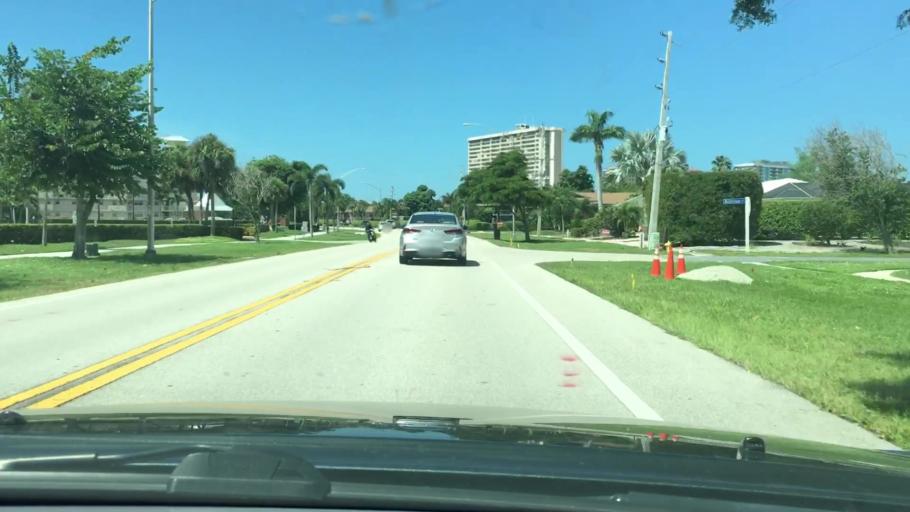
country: US
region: Florida
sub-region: Collier County
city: Marco
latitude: 25.9371
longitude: -81.7276
